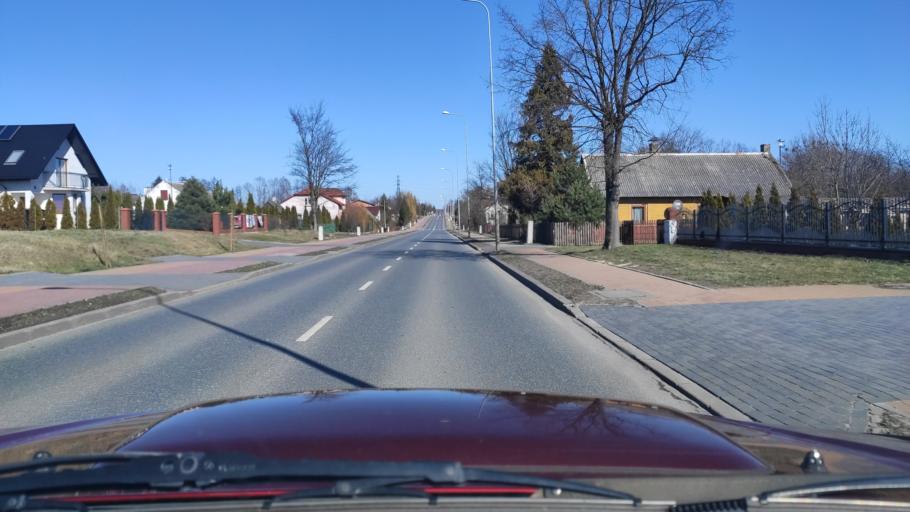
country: PL
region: Masovian Voivodeship
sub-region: Powiat zwolenski
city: Zwolen
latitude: 51.3641
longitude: 21.5839
